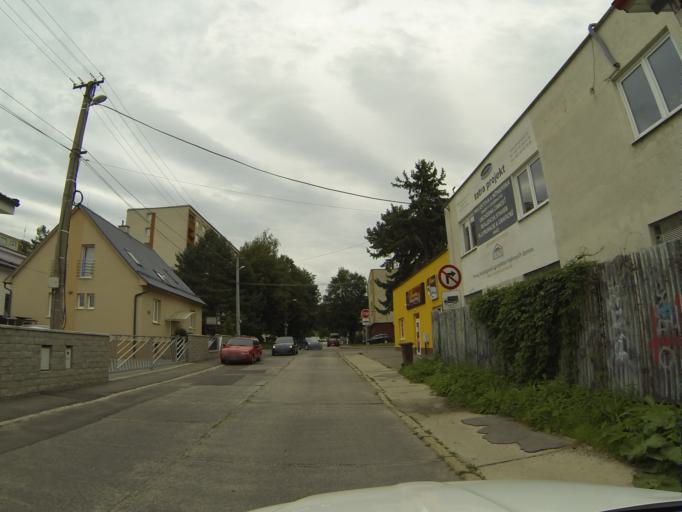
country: SK
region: Nitriansky
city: Prievidza
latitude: 48.7773
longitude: 18.6221
